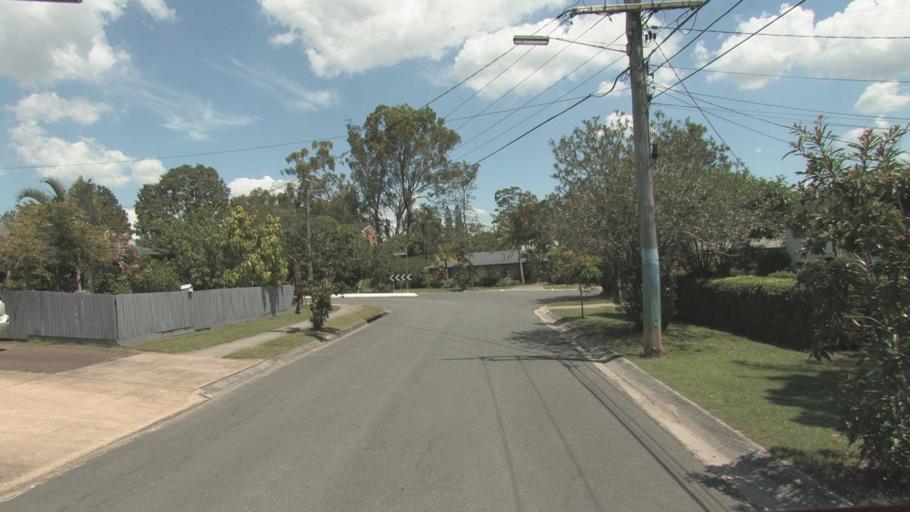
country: AU
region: Queensland
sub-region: Logan
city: Rochedale South
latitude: -27.5975
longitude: 153.1263
